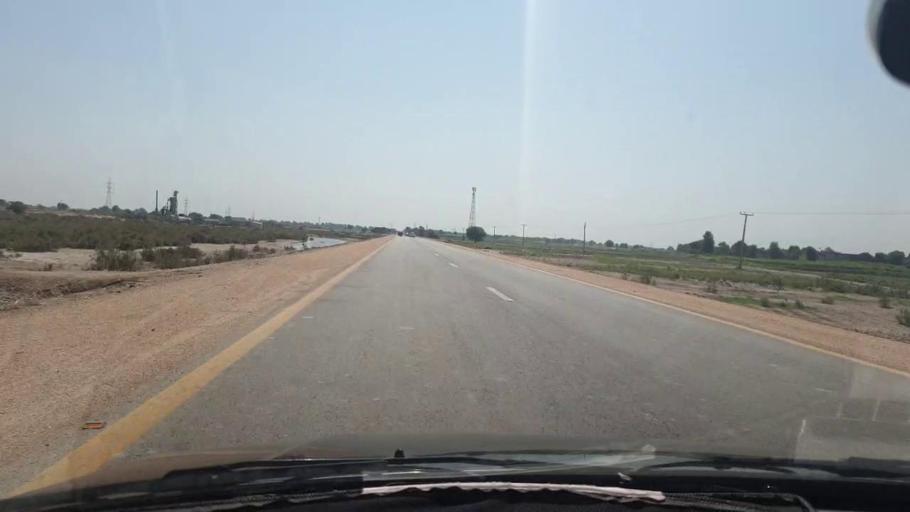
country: PK
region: Sindh
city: Chambar
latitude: 25.3366
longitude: 68.7959
